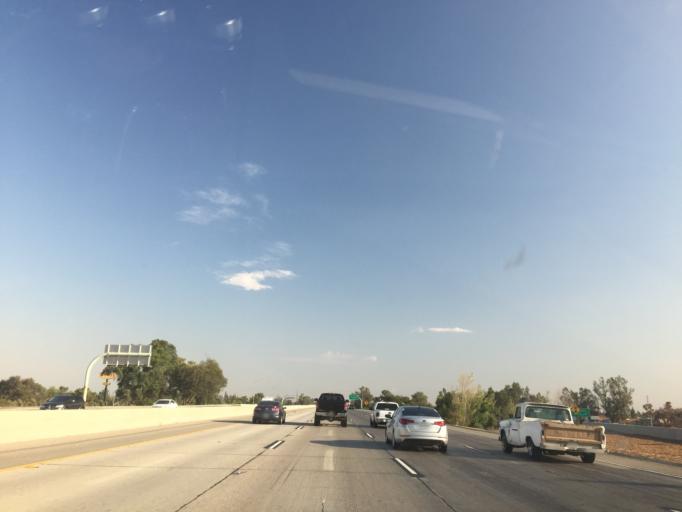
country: US
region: California
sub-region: Kern County
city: Bakersfield
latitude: 35.3859
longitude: -119.0447
